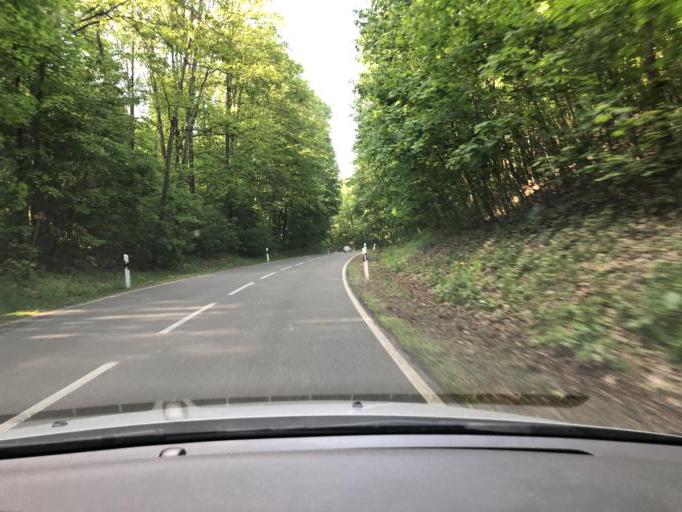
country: DE
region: Thuringia
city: Haselbach
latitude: 51.0644
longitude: 12.4383
